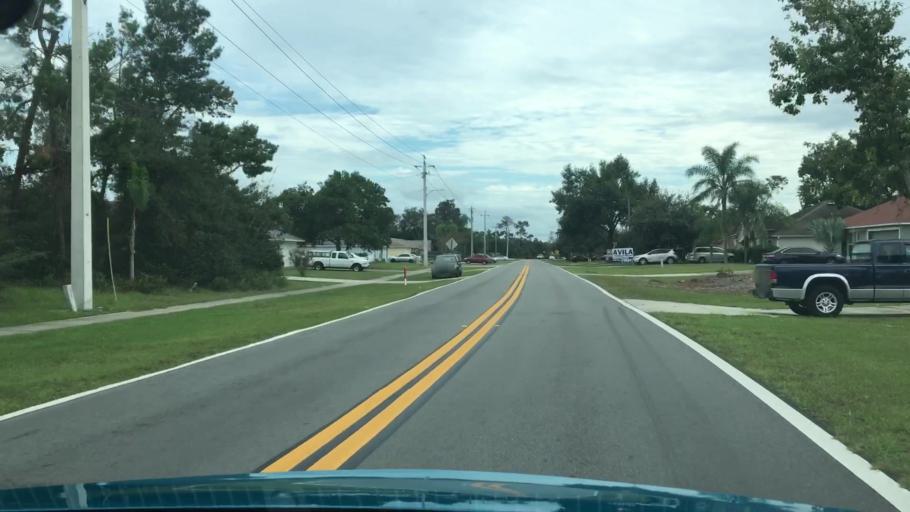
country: US
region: Florida
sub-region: Volusia County
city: Lake Helen
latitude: 28.9439
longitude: -81.1840
